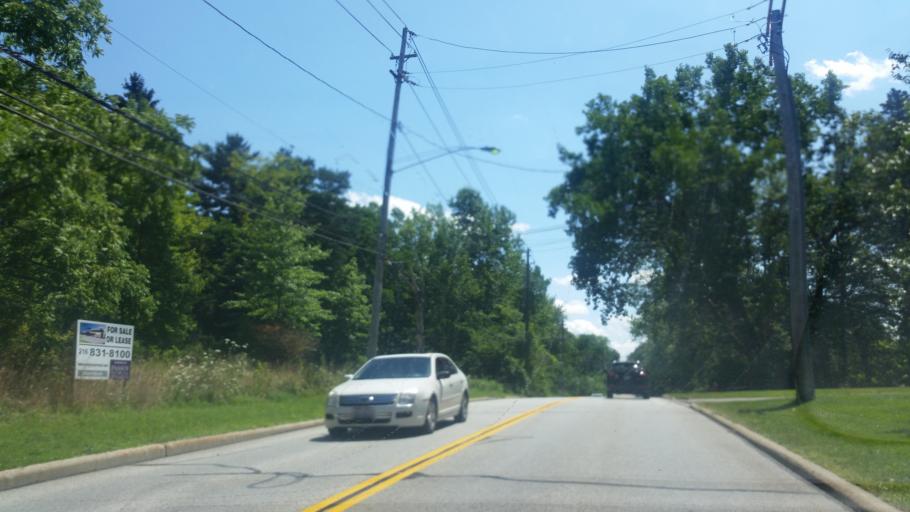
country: US
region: Ohio
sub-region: Cuyahoga County
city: Pepper Pike
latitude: 41.4609
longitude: -81.4634
